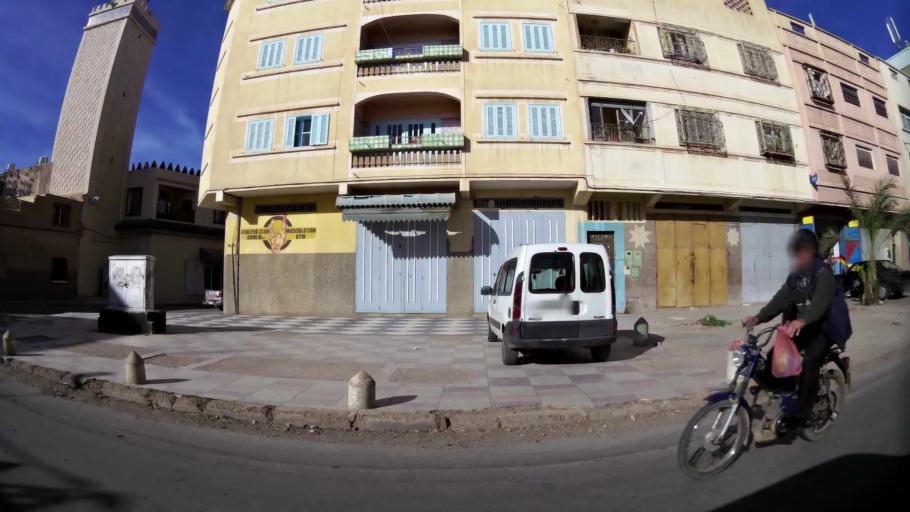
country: MA
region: Oriental
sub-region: Oujda-Angad
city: Oujda
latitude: 34.6748
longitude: -1.9026
